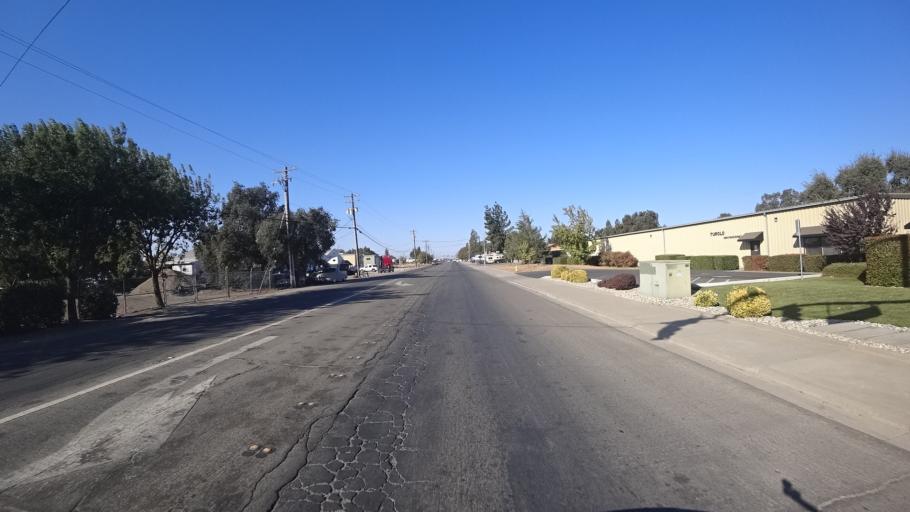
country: US
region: California
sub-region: Yolo County
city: Woodland
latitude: 38.6922
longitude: -121.7979
